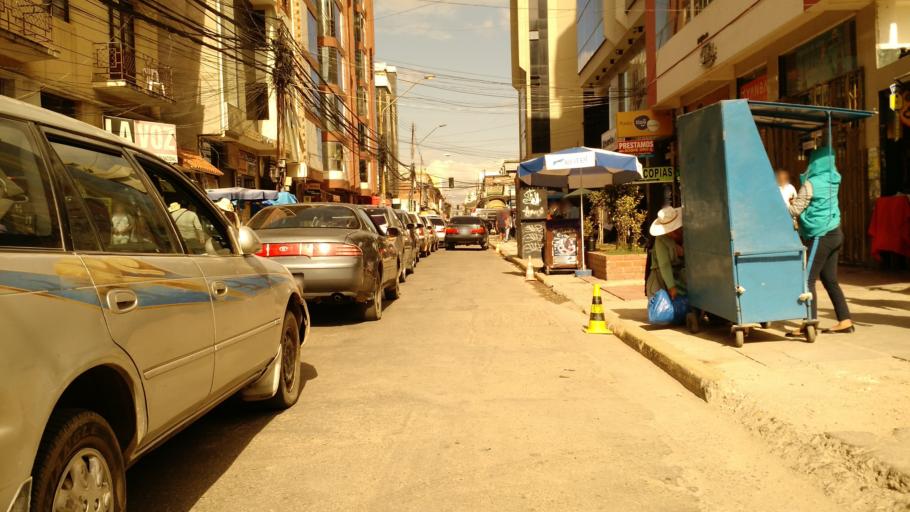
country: BO
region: Cochabamba
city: Cochabamba
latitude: -17.3947
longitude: -66.1532
